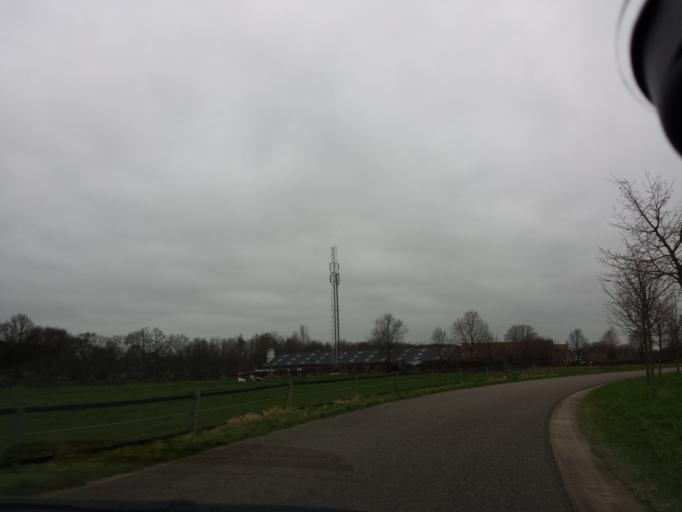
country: NL
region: Limburg
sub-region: Gemeente Roerdalen
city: Melick
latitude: 51.1813
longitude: 6.0227
